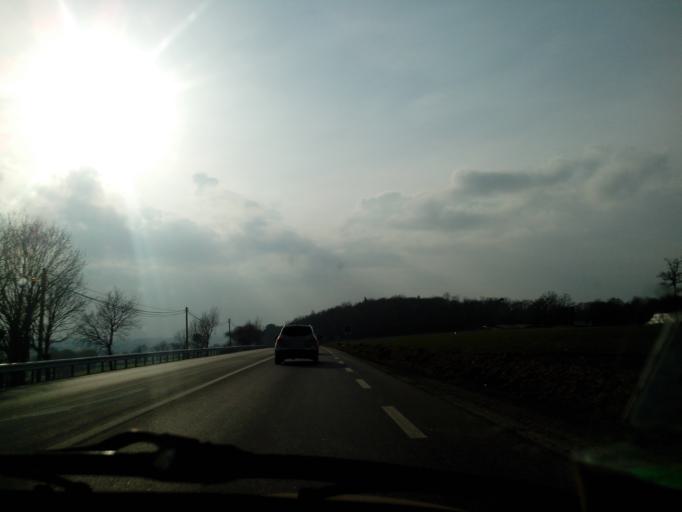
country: FR
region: Brittany
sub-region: Departement du Morbihan
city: Mauron
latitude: 48.0280
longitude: -2.3124
